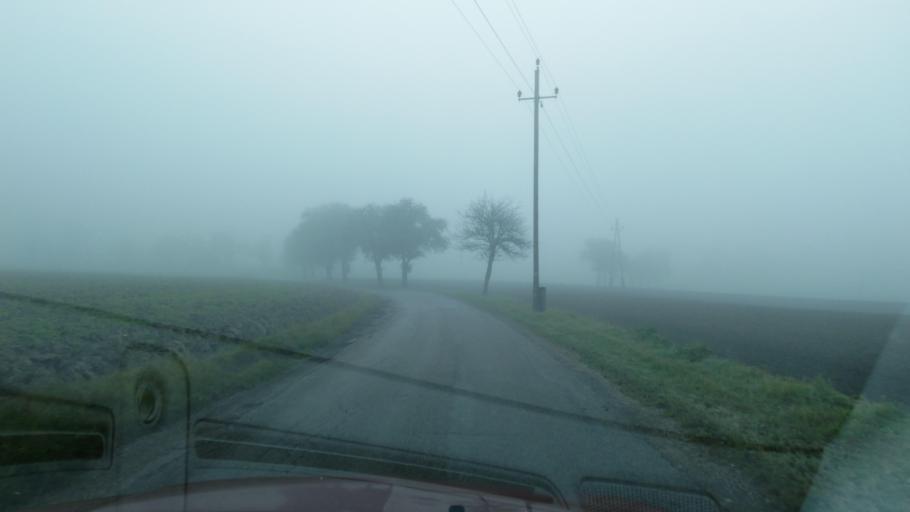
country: AT
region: Upper Austria
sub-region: Politischer Bezirk Grieskirchen
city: Bad Schallerbach
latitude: 48.2107
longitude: 13.8879
